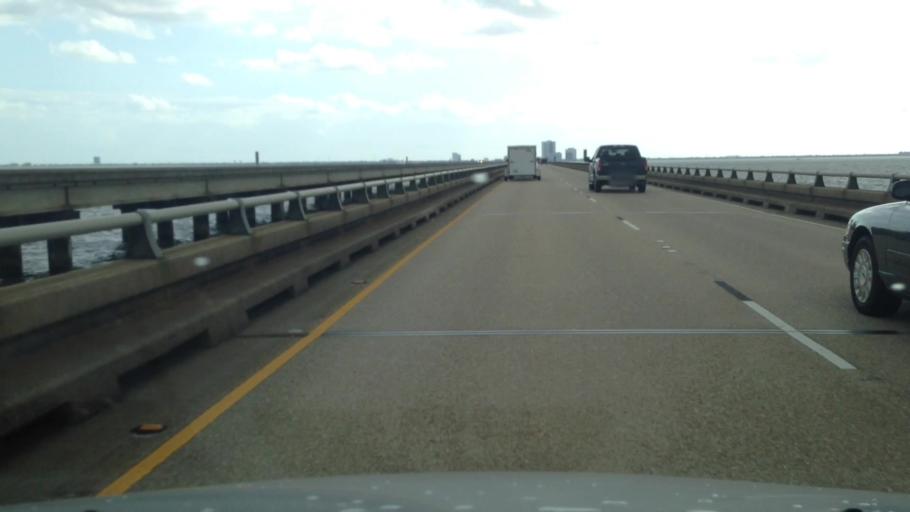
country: US
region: Louisiana
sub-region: Jefferson Parish
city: Metairie
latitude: 30.0688
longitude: -90.1458
